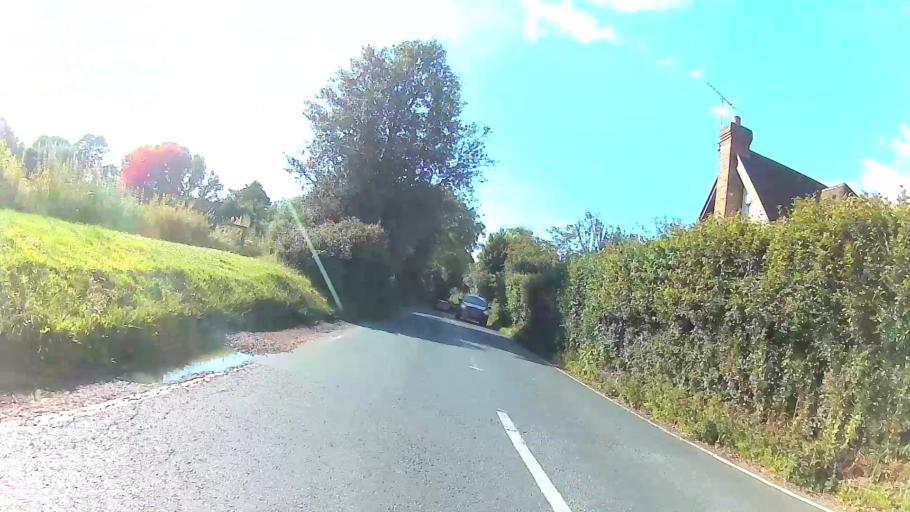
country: GB
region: England
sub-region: Essex
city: Kelvedon Hatch
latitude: 51.6732
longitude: 0.2920
